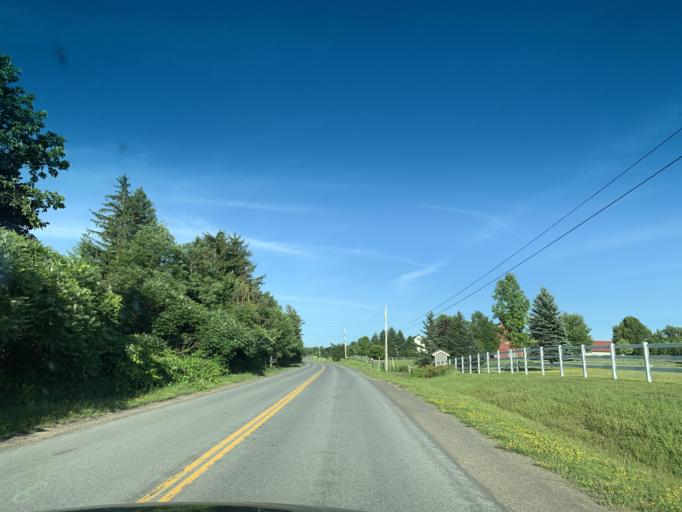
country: US
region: New York
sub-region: Oneida County
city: Clinton
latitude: 43.0547
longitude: -75.4561
